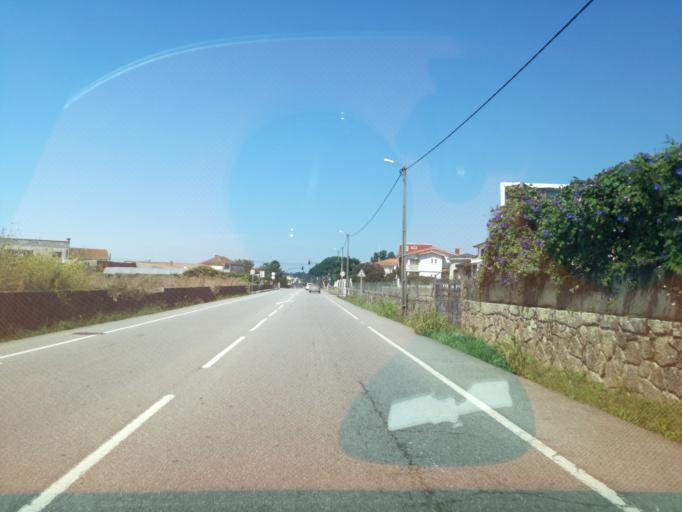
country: PT
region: Braga
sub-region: Esposende
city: Apulia
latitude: 41.4724
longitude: -8.7466
